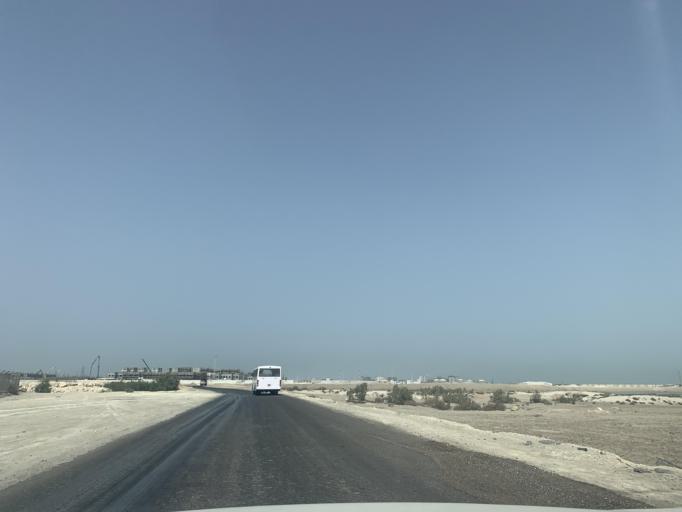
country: BH
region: Northern
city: Sitrah
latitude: 26.1560
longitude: 50.6276
